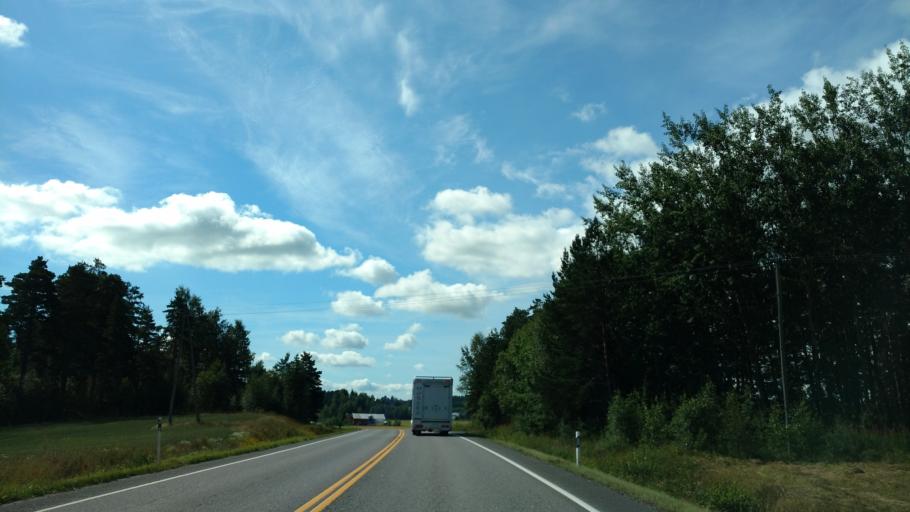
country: FI
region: Varsinais-Suomi
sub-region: Salo
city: Pernioe
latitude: 60.2119
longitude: 23.1113
